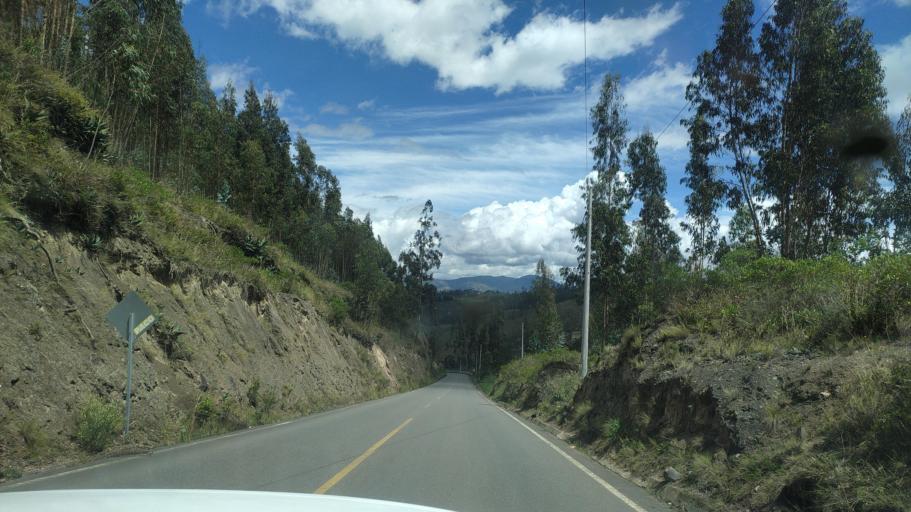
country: EC
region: Chimborazo
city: Riobamba
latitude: -1.6604
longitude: -78.5825
